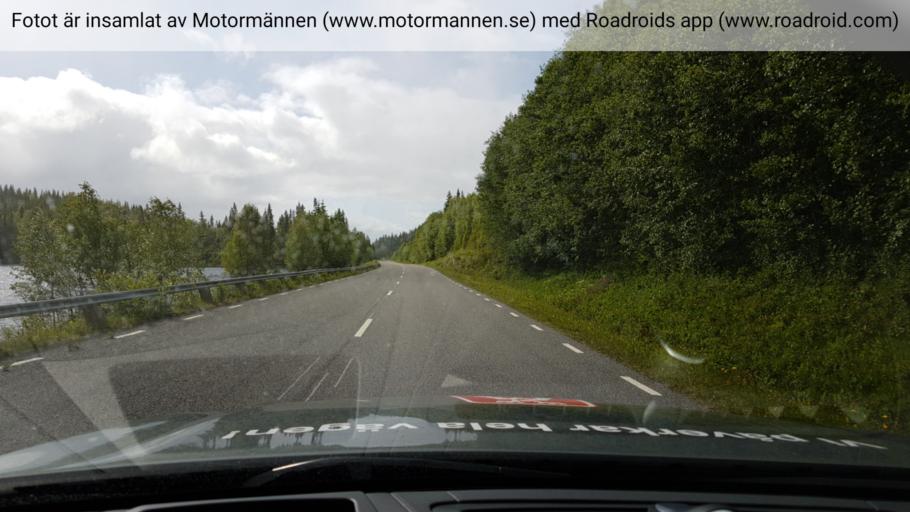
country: SE
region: Jaemtland
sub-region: Are Kommun
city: Are
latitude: 63.6810
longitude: 13.0288
